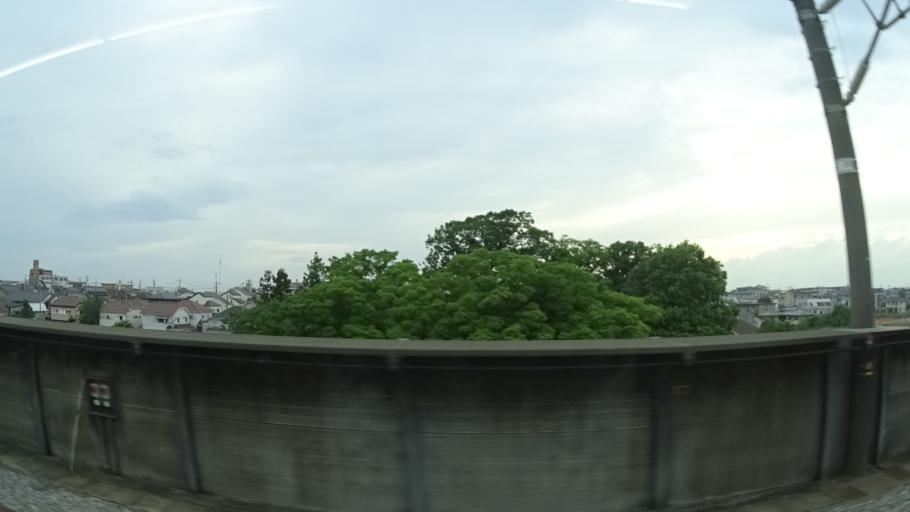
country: JP
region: Saitama
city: Yono
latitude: 35.8656
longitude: 139.6323
